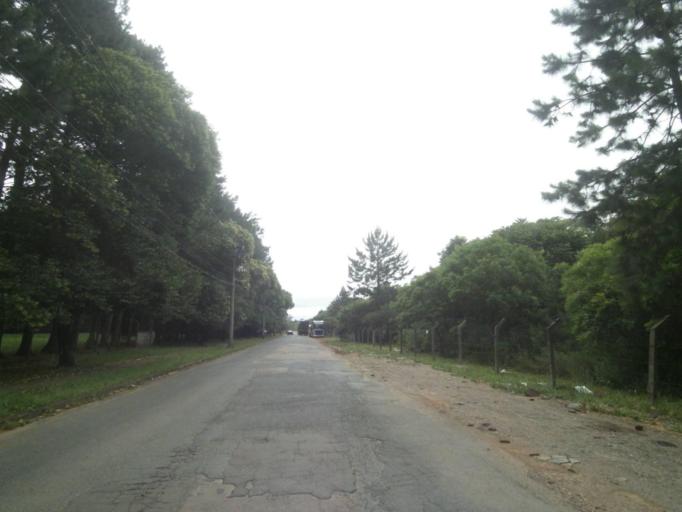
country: BR
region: Parana
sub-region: Araucaria
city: Araucaria
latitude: -25.5360
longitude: -49.3310
